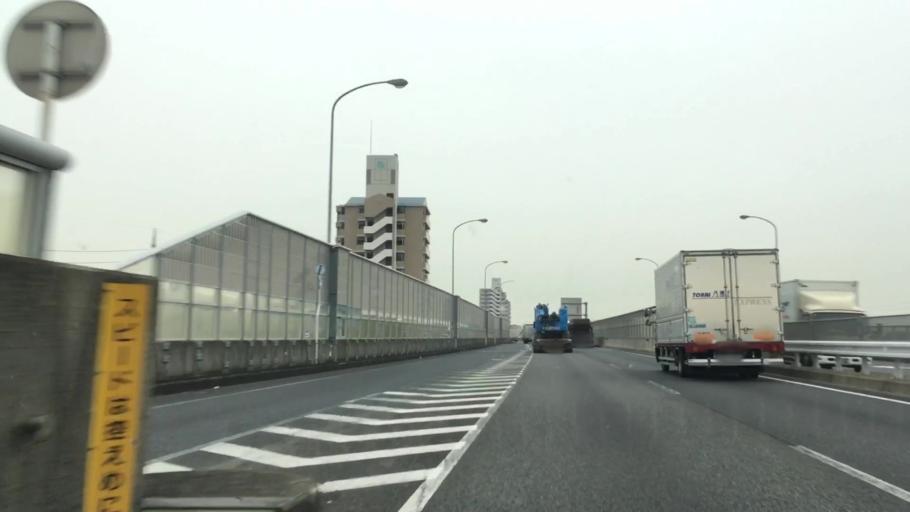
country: JP
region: Aichi
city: Chiryu
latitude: 34.9758
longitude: 137.0356
